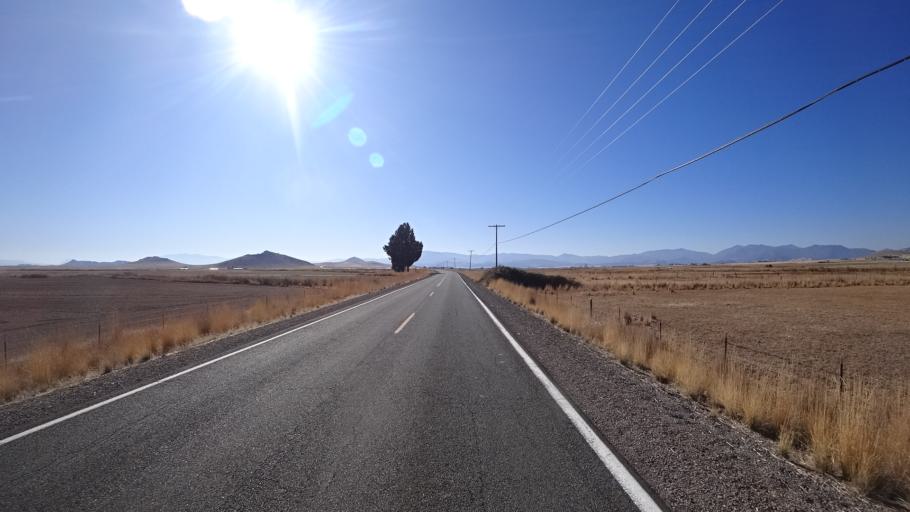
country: US
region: California
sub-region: Siskiyou County
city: Montague
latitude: 41.7671
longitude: -122.4840
